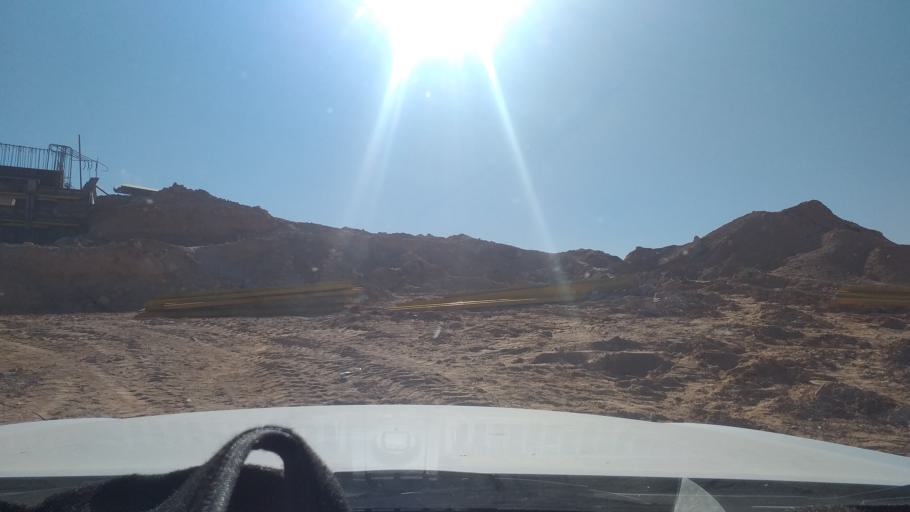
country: TN
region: Madanin
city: Medenine
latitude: 33.3177
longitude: 10.6067
